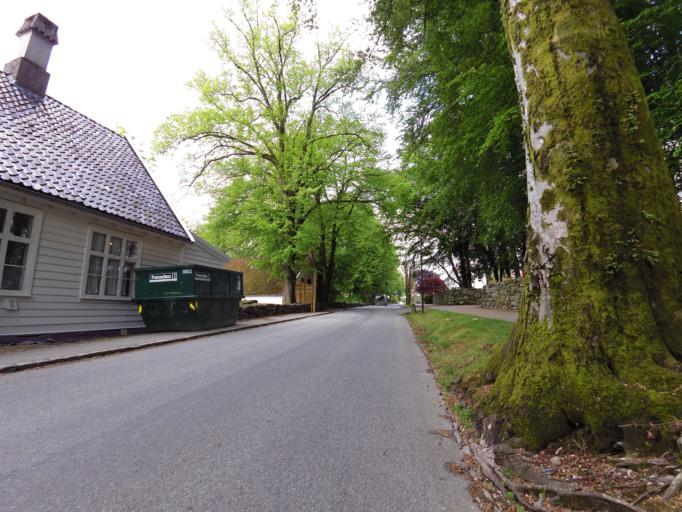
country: NO
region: Rogaland
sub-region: Stavanger
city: Stavanger
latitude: 58.9662
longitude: 5.7215
